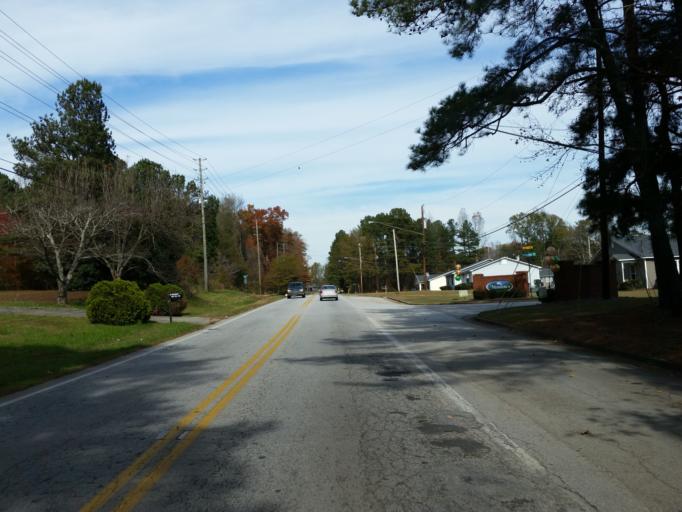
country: US
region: Georgia
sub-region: Douglas County
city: Lithia Springs
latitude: 33.7365
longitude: -84.6671
